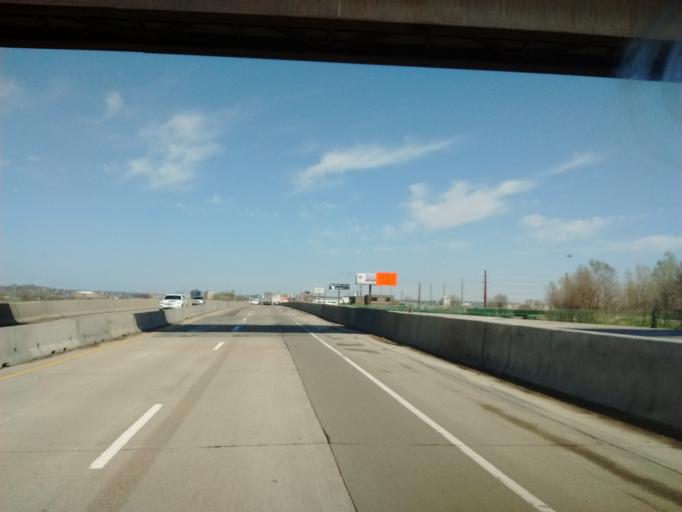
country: US
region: Nebraska
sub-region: Dakota County
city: South Sioux City
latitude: 42.4750
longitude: -96.3837
